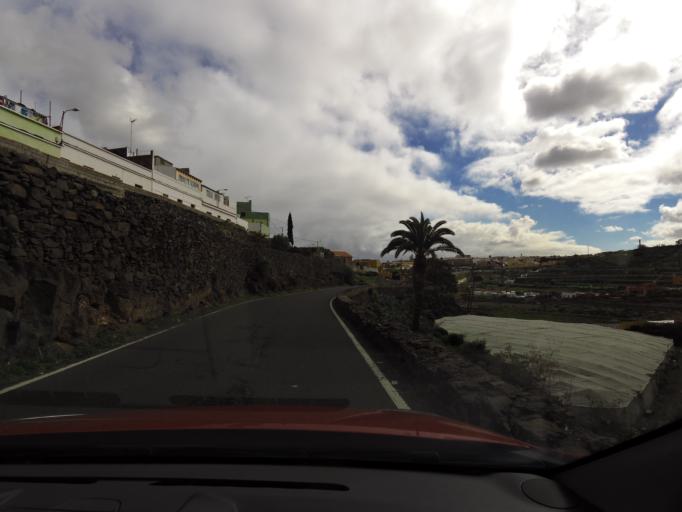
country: ES
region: Canary Islands
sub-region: Provincia de Las Palmas
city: Telde
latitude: 28.0074
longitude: -15.4223
